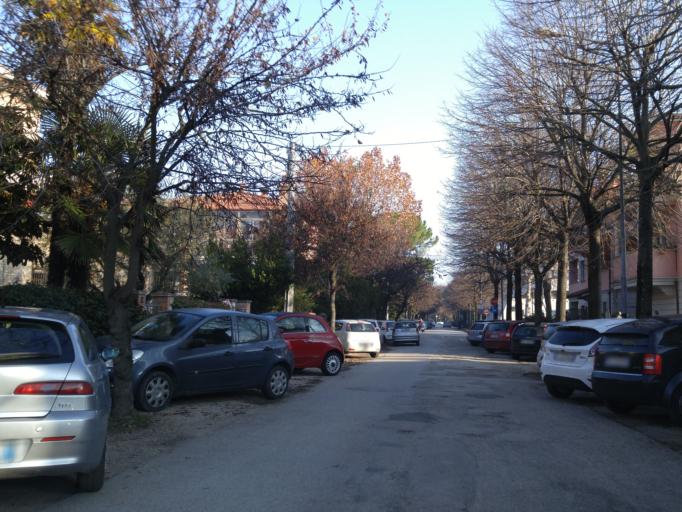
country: IT
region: The Marches
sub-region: Provincia di Pesaro e Urbino
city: Fano
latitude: 43.8377
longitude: 13.0098
